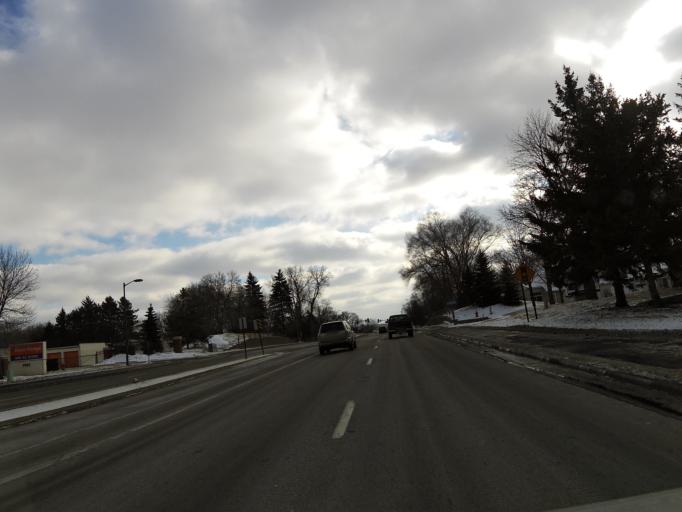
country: US
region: Minnesota
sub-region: Hennepin County
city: Eden Prairie
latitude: 44.8598
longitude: -93.4855
